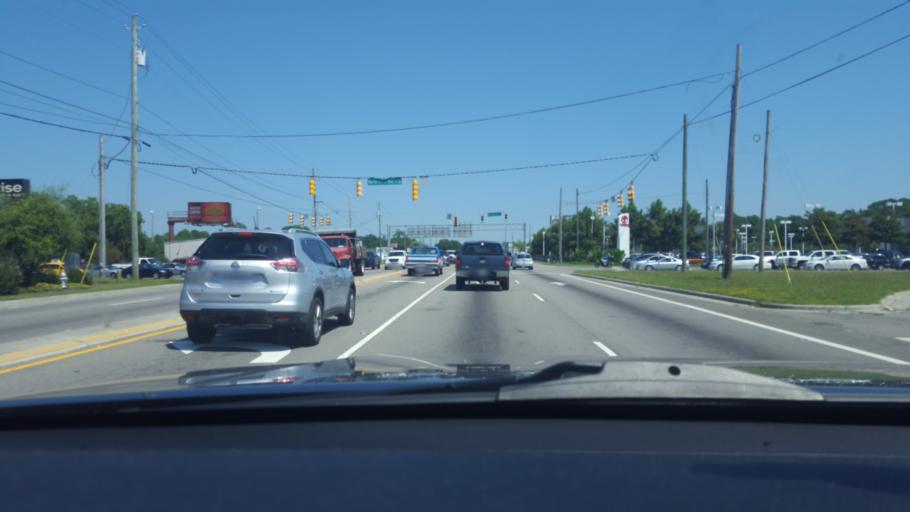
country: US
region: North Carolina
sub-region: New Hanover County
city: Kings Grant
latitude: 34.2477
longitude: -77.8645
